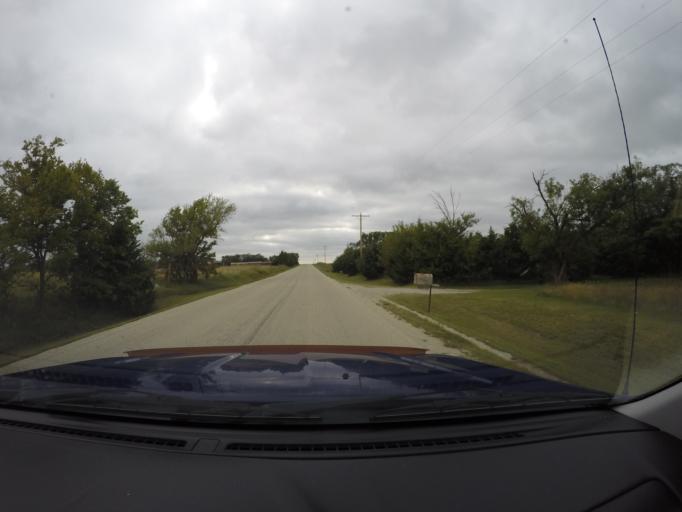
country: US
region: Kansas
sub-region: Dickinson County
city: Herington
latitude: 38.7975
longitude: -96.7531
